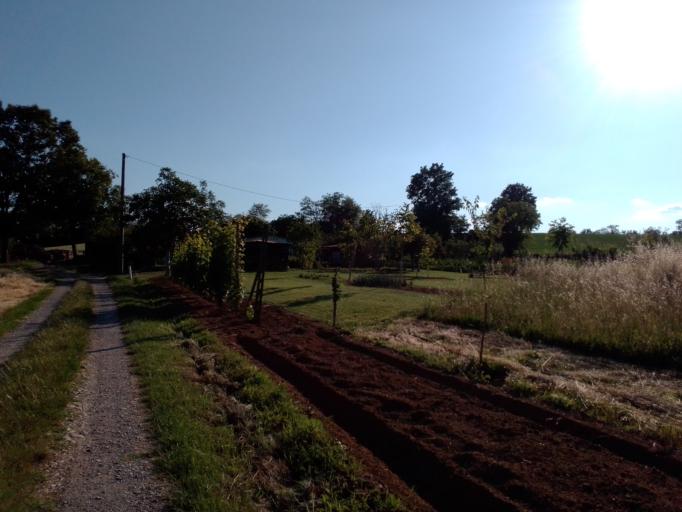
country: IT
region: Emilia-Romagna
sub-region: Provincia di Piacenza
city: Borgonovo Valtidone
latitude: 45.0010
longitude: 9.4350
